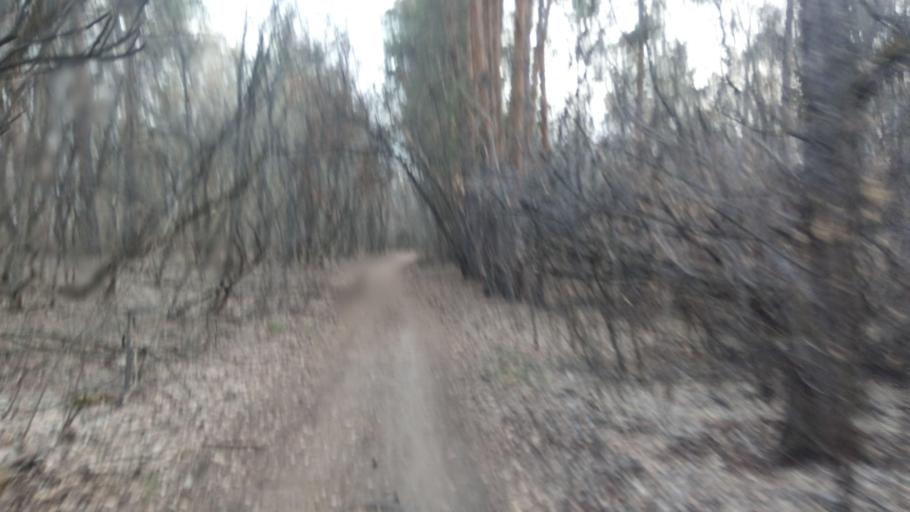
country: RU
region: Chelyabinsk
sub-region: Gorod Chelyabinsk
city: Chelyabinsk
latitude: 55.1455
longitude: 61.3470
